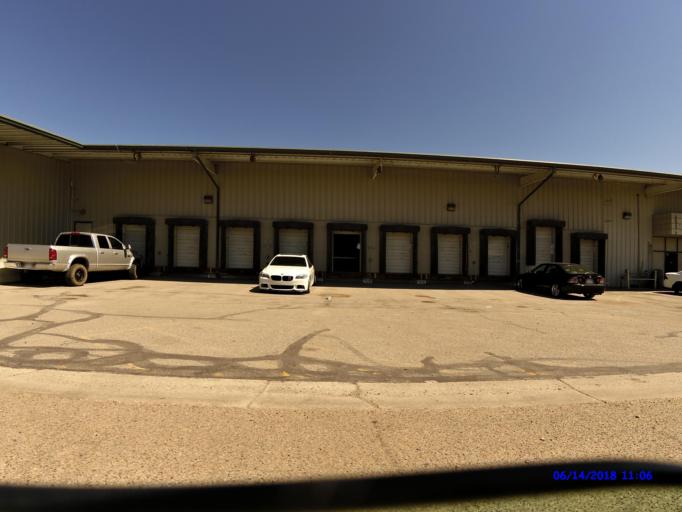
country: US
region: Utah
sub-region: Weber County
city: Ogden
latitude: 41.2149
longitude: -112.0052
